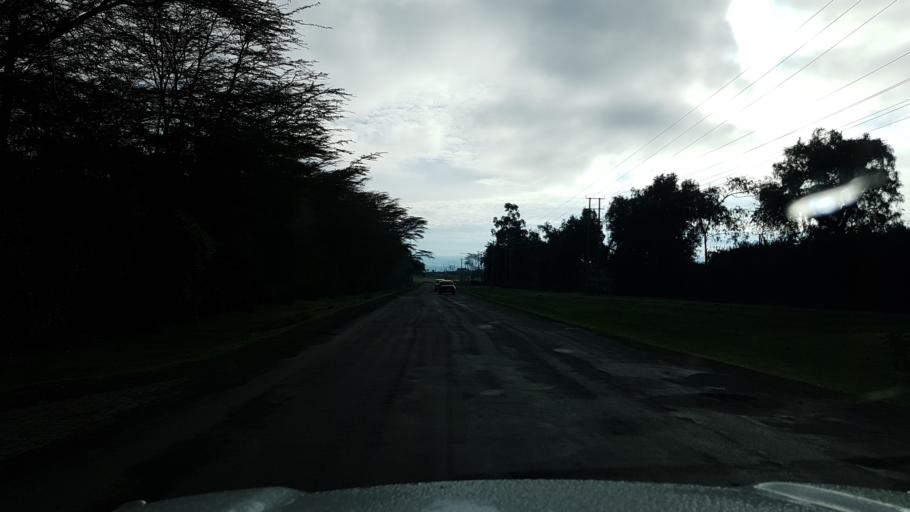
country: KE
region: Nakuru
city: Naivasha
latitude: -0.8253
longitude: 36.3792
